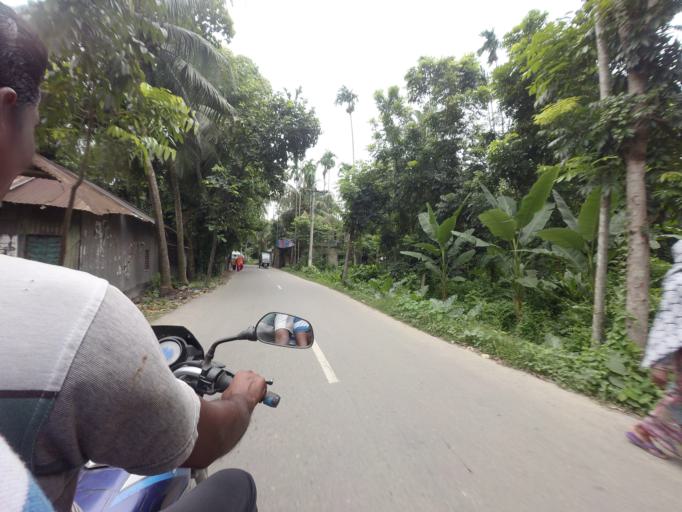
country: BD
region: Khulna
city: Kalia
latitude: 23.1783
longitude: 89.6478
